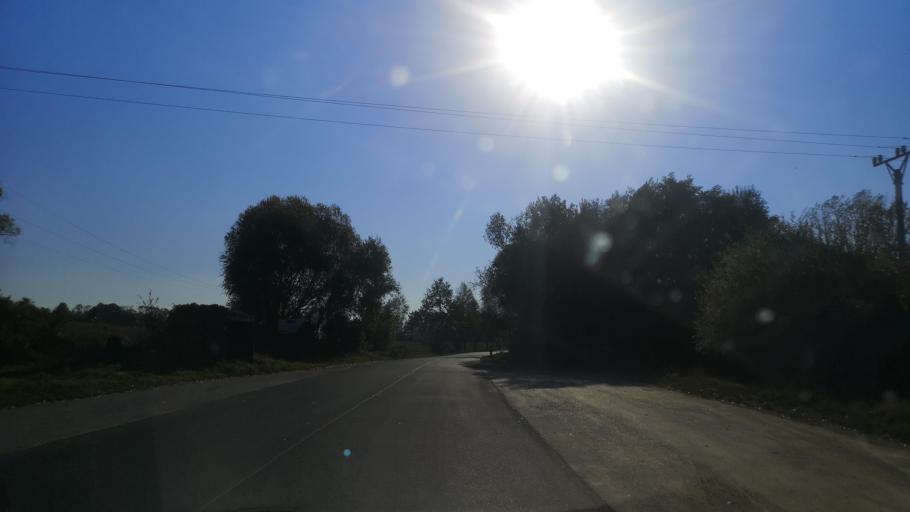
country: SK
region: Nitriansky
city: Zlate Moravce
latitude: 48.4288
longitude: 18.4263
